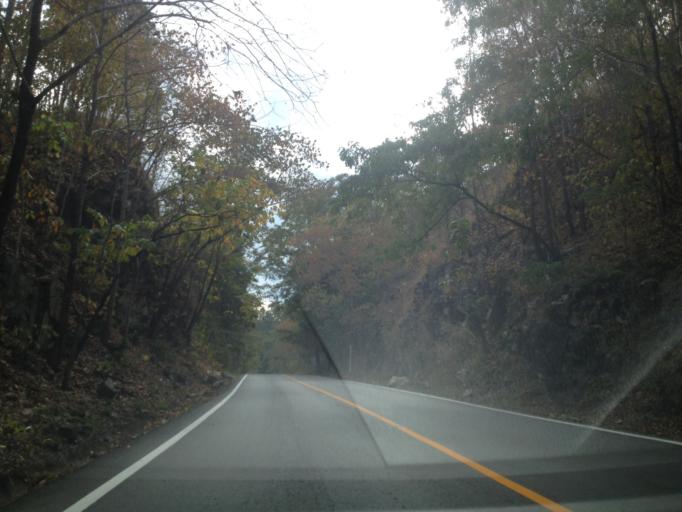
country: TH
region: Chiang Mai
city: Hot
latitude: 18.1922
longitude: 98.4503
